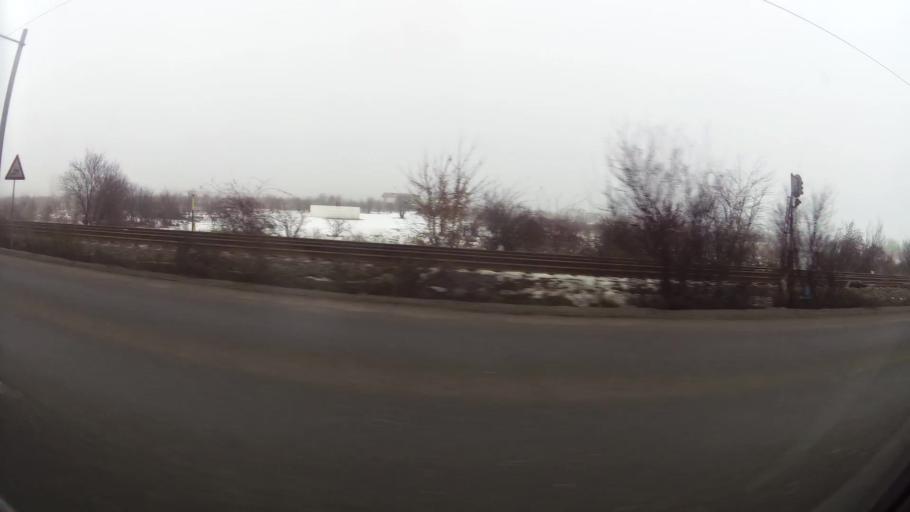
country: RO
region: Ilfov
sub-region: Comuna Bragadiru
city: Bragadiru
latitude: 44.3951
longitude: 25.9825
